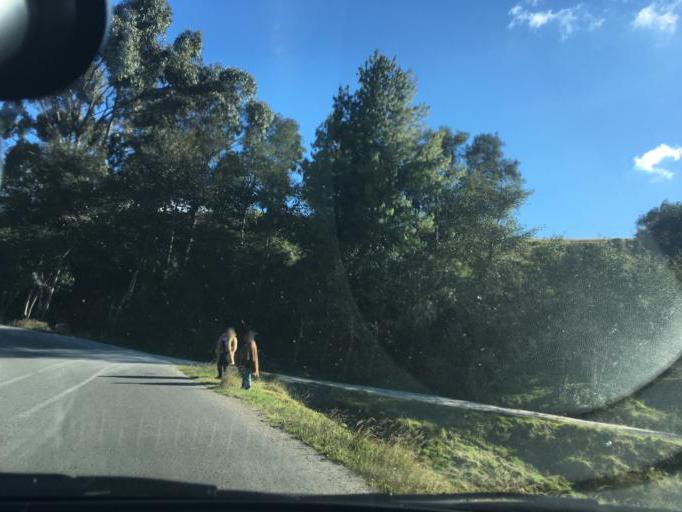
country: CO
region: Boyaca
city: Pesca
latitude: 5.5233
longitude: -72.9769
